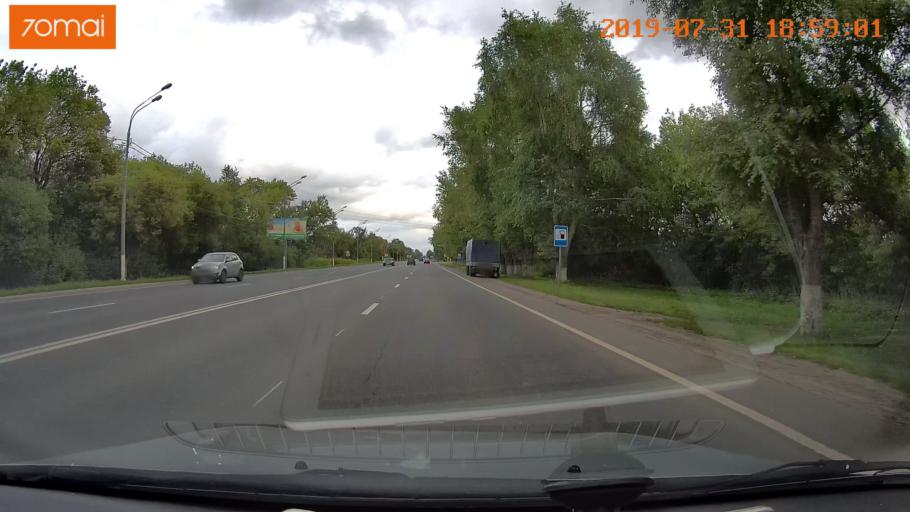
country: RU
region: Moskovskaya
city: Raduzhnyy
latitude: 55.1422
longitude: 38.7112
